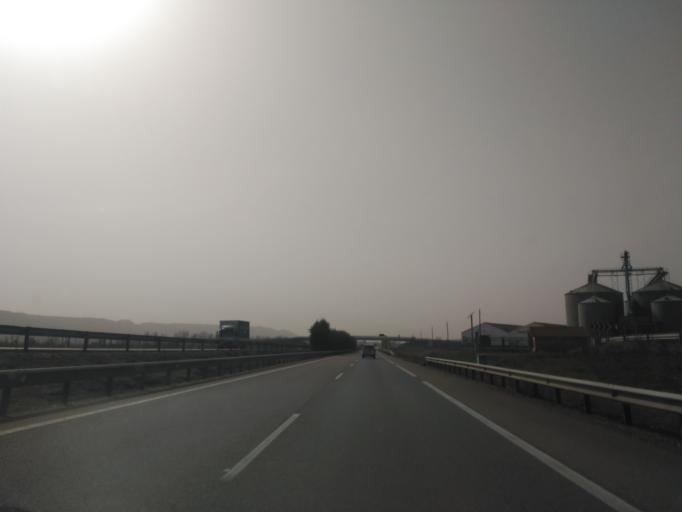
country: ES
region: Castille and Leon
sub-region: Provincia de Valladolid
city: Cubillas de Santa Marta
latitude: 41.7817
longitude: -4.6134
